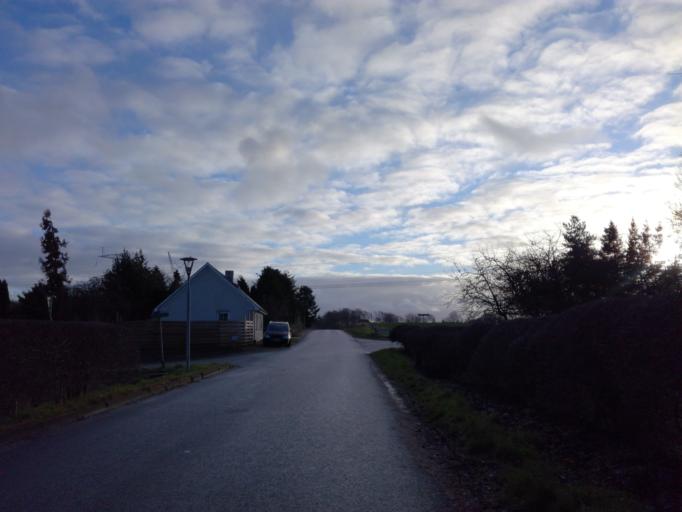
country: DK
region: South Denmark
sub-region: Fredericia Kommune
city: Taulov
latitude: 55.5563
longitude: 9.6024
